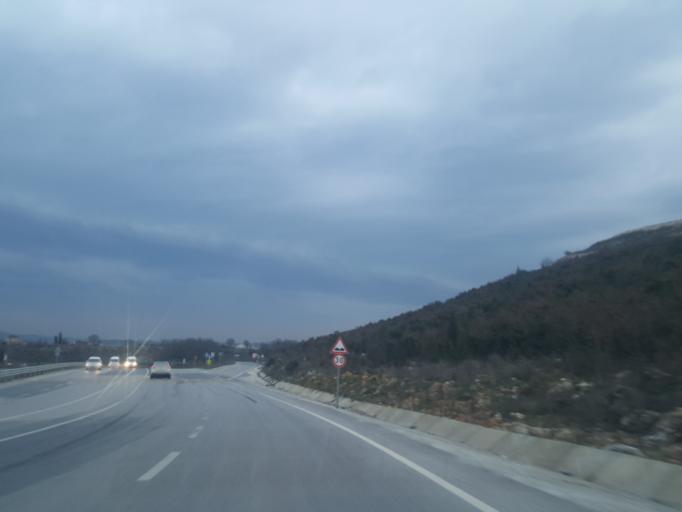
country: TR
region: Kocaeli
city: Tavsanli
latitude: 40.8393
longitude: 29.5522
